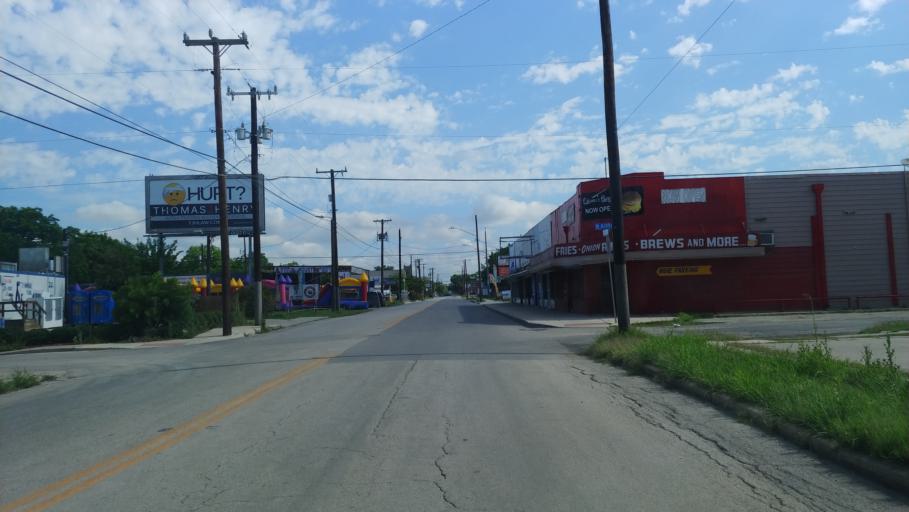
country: US
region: Texas
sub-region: Bexar County
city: San Antonio
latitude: 29.4503
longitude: -98.5243
